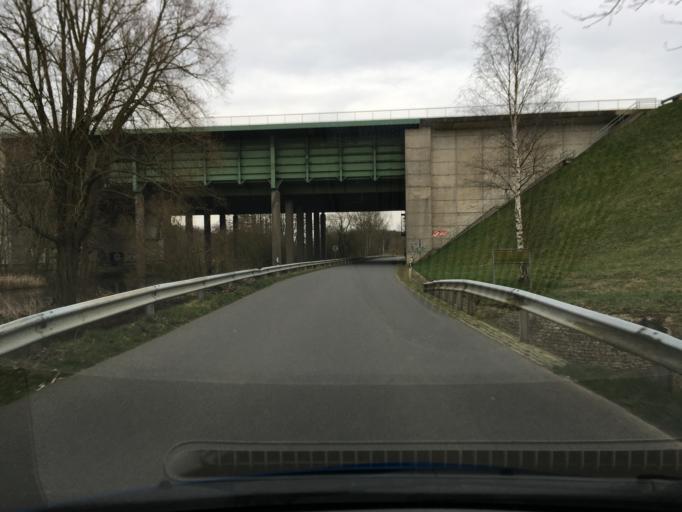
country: DE
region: Lower Saxony
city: Bad Bevensen
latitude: 53.0561
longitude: 10.5973
